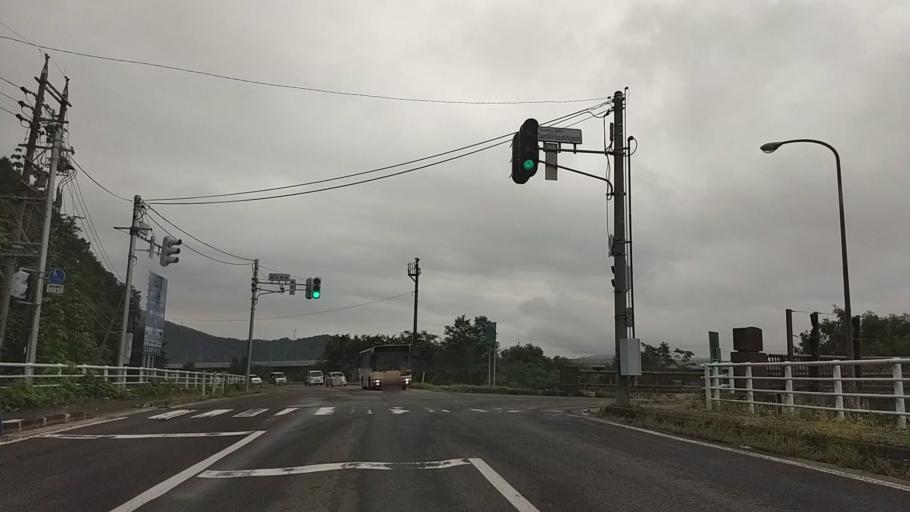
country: JP
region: Nagano
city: Iiyama
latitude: 36.8412
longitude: 138.3663
